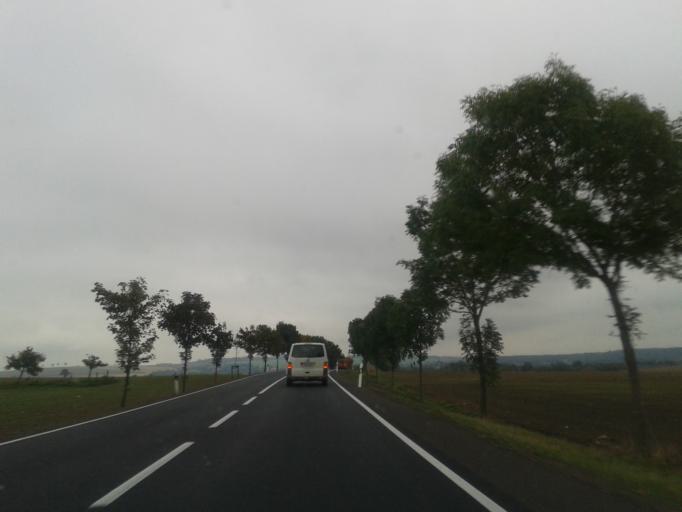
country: DE
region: Saxony
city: Wilsdruff
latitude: 51.0507
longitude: 13.4552
